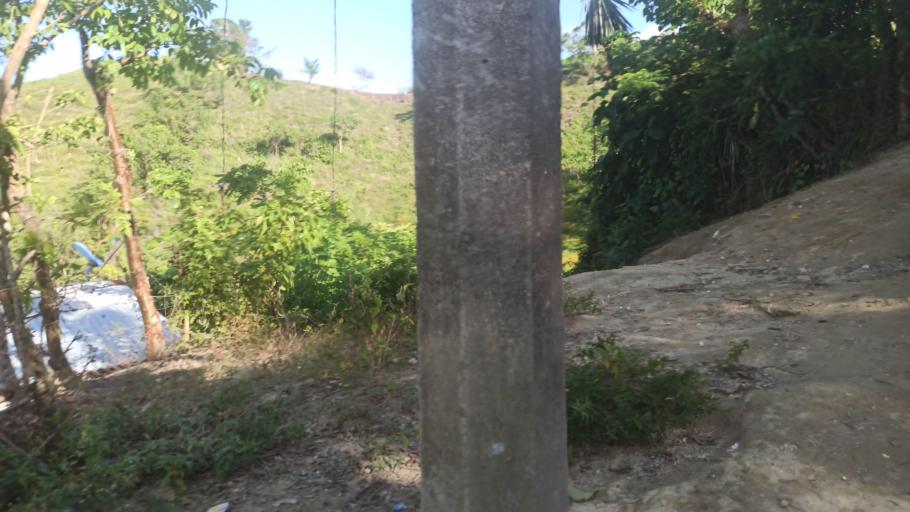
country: MX
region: Veracruz
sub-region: Poza Rica de Hidalgo
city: El Mollejon
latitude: 20.5561
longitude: -97.3960
